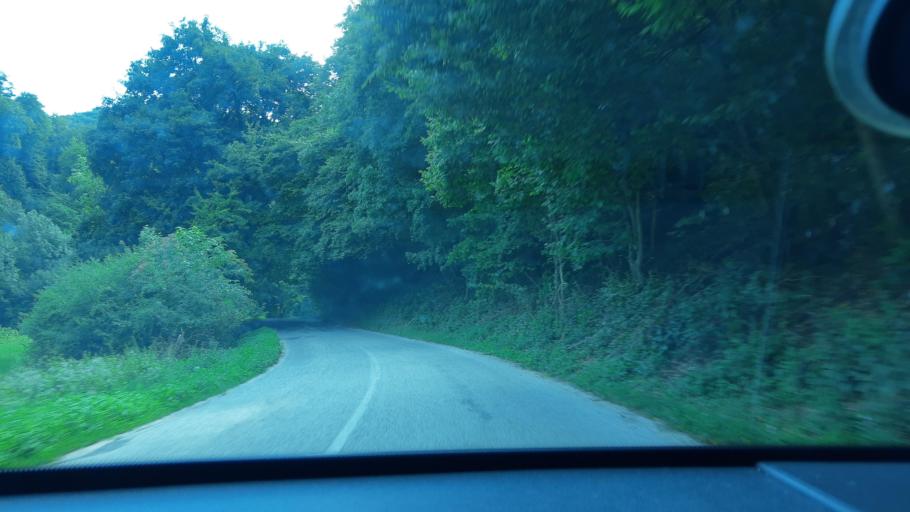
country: SK
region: Trnavsky
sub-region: Okres Trnava
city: Piestany
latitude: 48.6375
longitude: 17.9276
